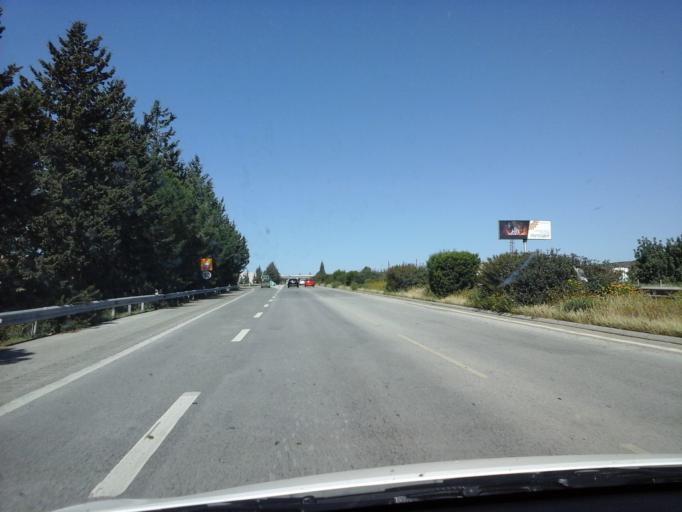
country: CY
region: Limassol
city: Ypsonas
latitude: 34.6932
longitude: 32.9717
